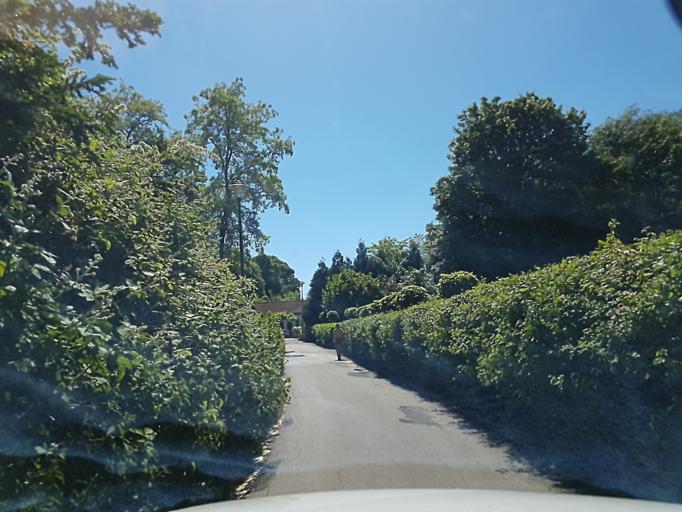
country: DE
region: North Rhine-Westphalia
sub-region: Regierungsbezirk Dusseldorf
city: Meerbusch
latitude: 51.3215
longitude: 6.7369
